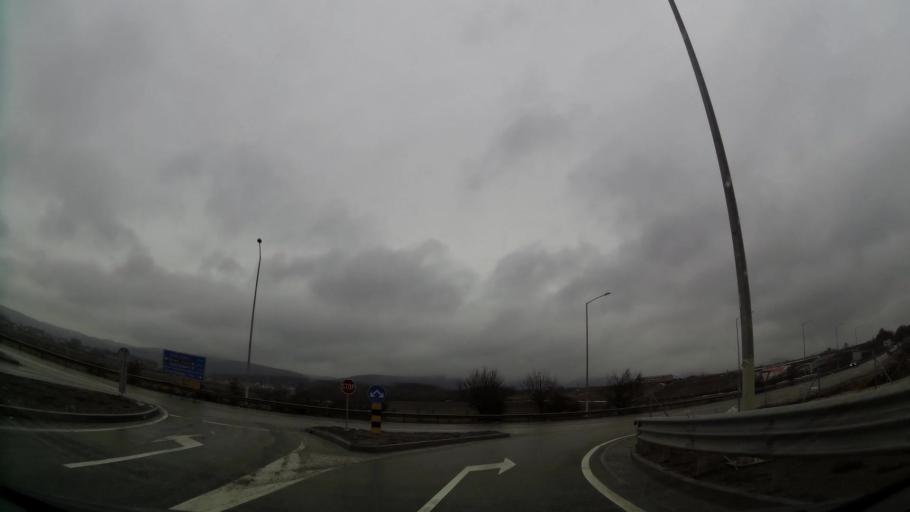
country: XK
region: Ferizaj
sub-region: Komuna e Kacanikut
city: Kacanik
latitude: 42.2742
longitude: 21.2177
